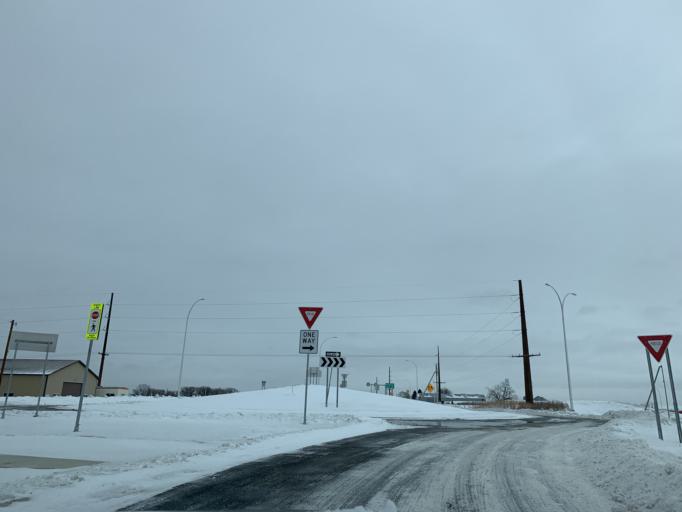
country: US
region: Minnesota
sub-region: Carver County
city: Carver
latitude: 44.7911
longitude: -93.6344
